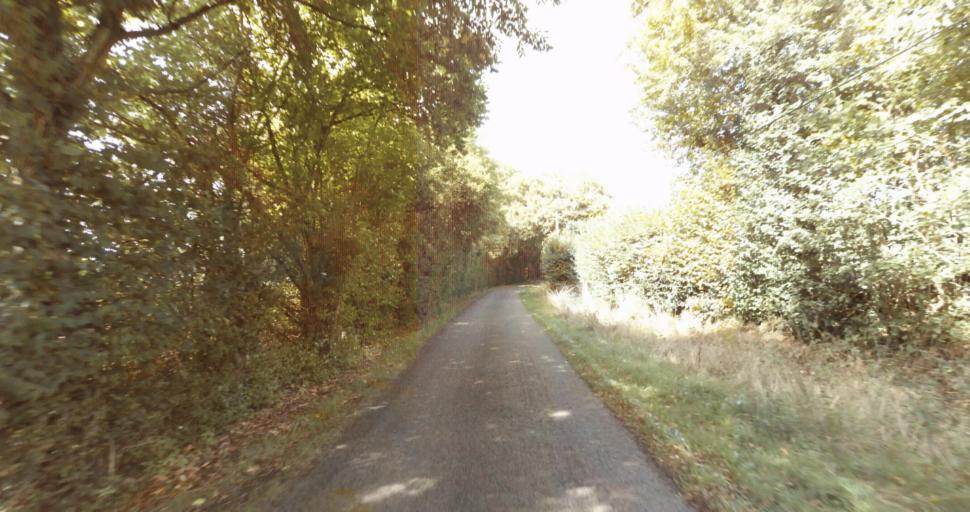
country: FR
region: Lower Normandy
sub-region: Departement de l'Orne
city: Sees
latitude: 48.7141
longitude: 0.1742
